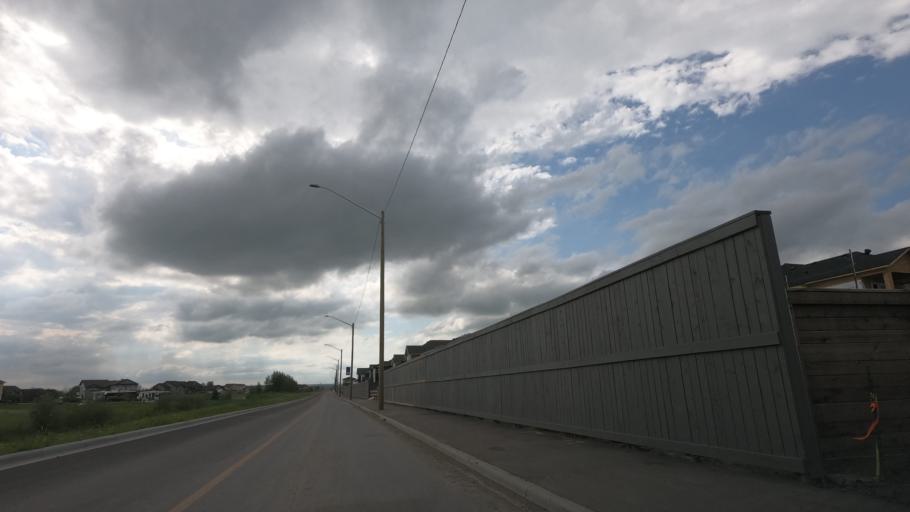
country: CA
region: Alberta
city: Airdrie
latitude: 51.2564
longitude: -113.9824
